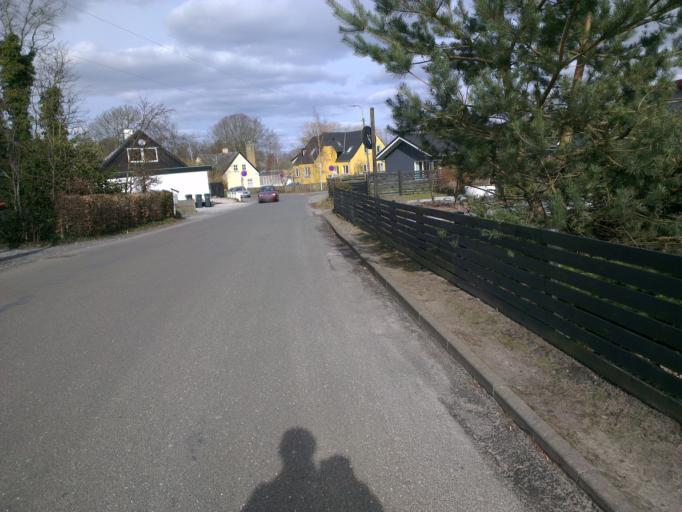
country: DK
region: Capital Region
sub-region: Frederikssund Kommune
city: Skibby
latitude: 55.7814
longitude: 12.0150
